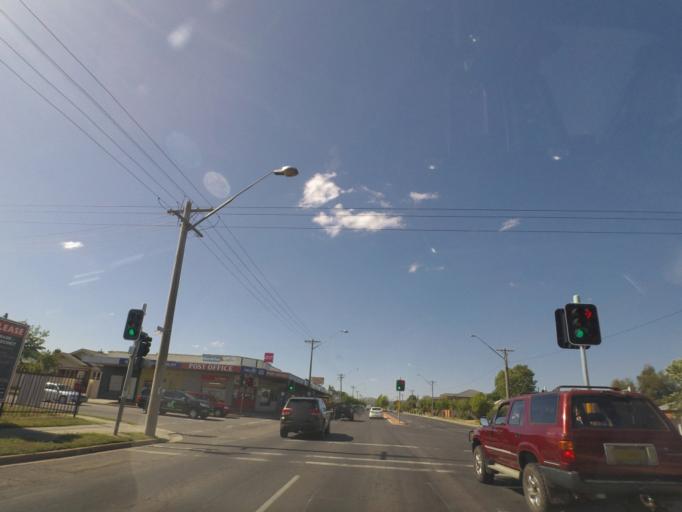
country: AU
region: New South Wales
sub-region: Albury Municipality
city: North Albury
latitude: -36.0632
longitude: 146.9315
